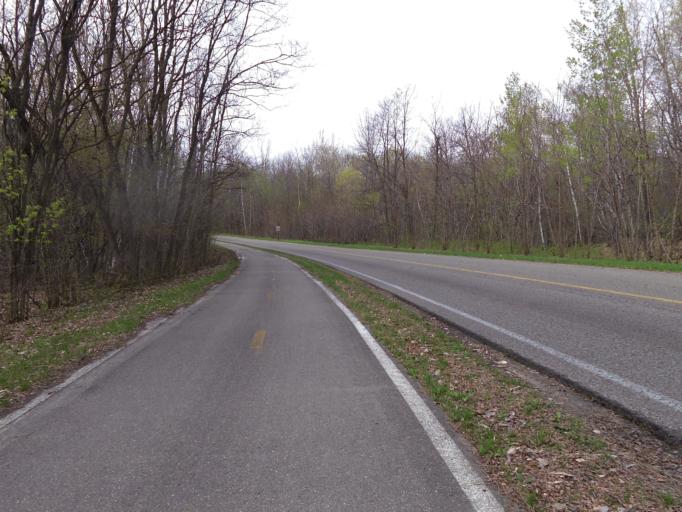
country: CA
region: Quebec
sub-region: Laurentides
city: Sainte-Marthe-sur-le-Lac
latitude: 45.4972
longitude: -74.0060
